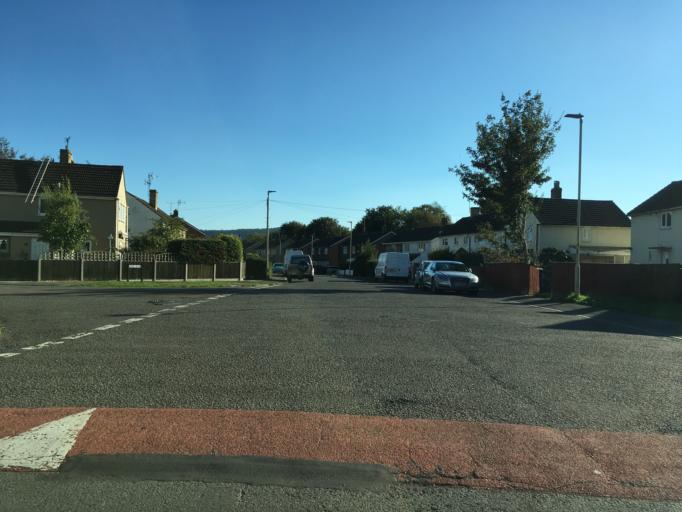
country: GB
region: England
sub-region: Gloucestershire
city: Stonehouse
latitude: 51.7479
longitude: -2.2910
